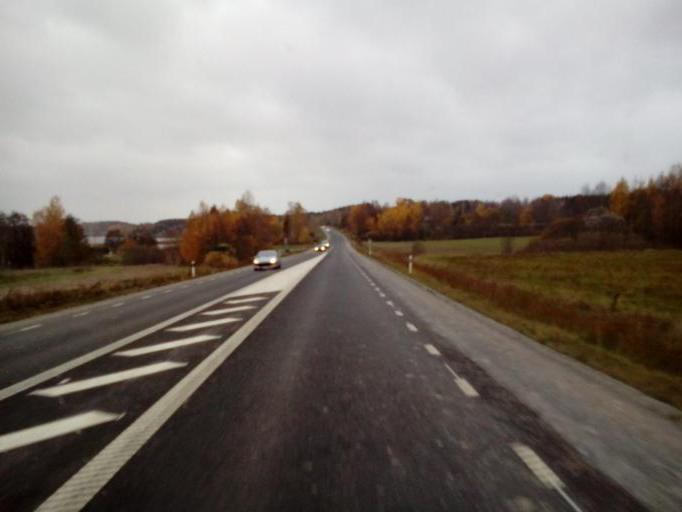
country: SE
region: OErebro
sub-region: Degerfors Kommun
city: Degerfors
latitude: 59.2808
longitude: 14.4556
